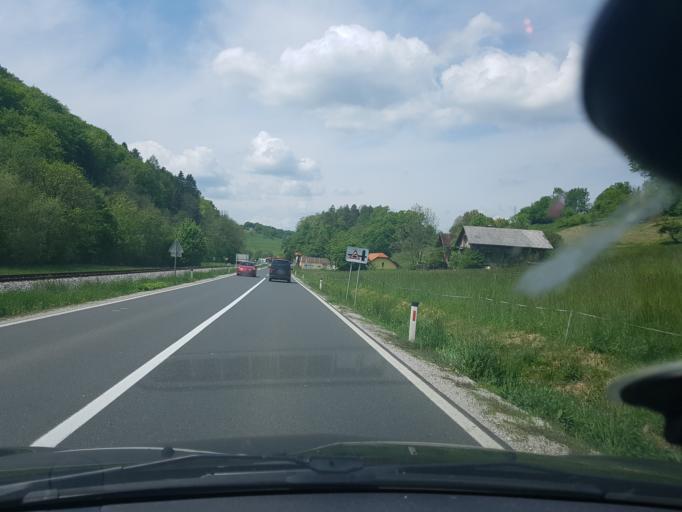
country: SI
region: Rogaska Slatina
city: Rogaska Slatina
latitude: 46.2427
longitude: 15.5818
